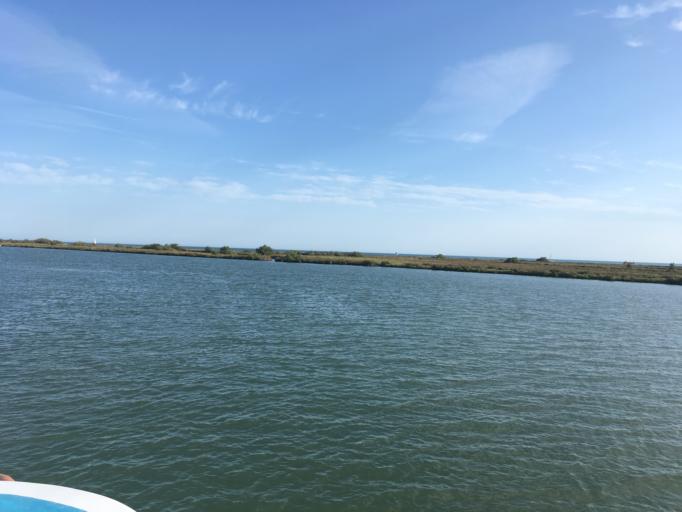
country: FR
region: Provence-Alpes-Cote d'Azur
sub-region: Departement des Bouches-du-Rhone
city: Saintes-Maries-de-la-Mer
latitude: 43.4569
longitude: 4.3906
